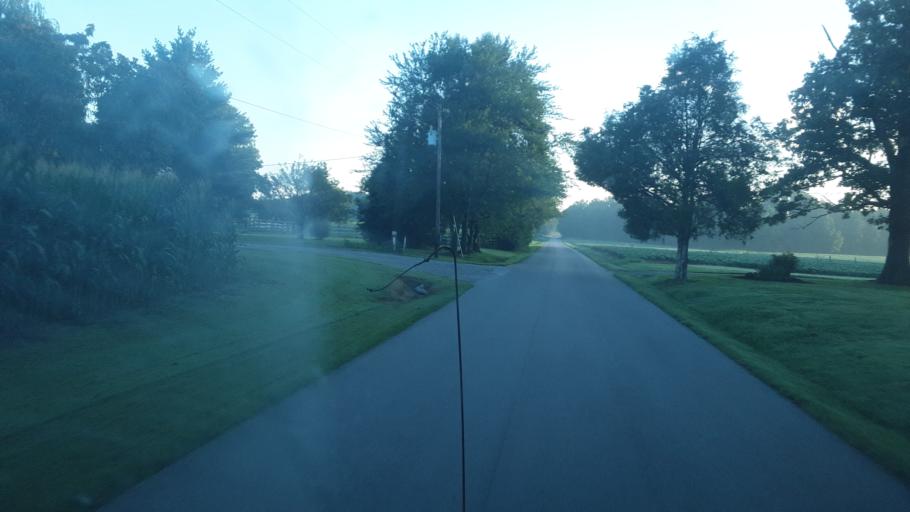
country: US
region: Kentucky
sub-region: Todd County
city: Guthrie
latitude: 36.7255
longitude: -87.1688
